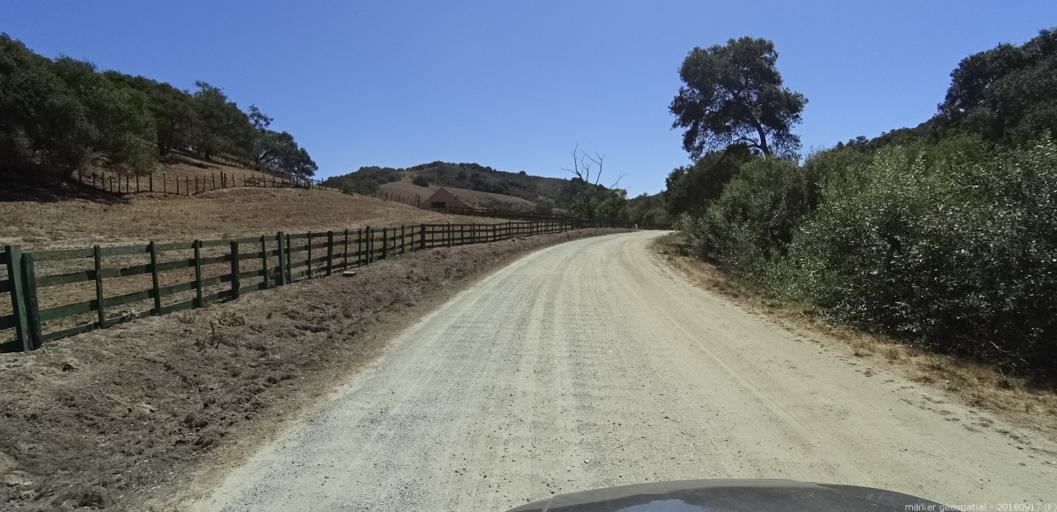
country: US
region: California
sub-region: San Benito County
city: Aromas
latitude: 36.8380
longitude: -121.6299
